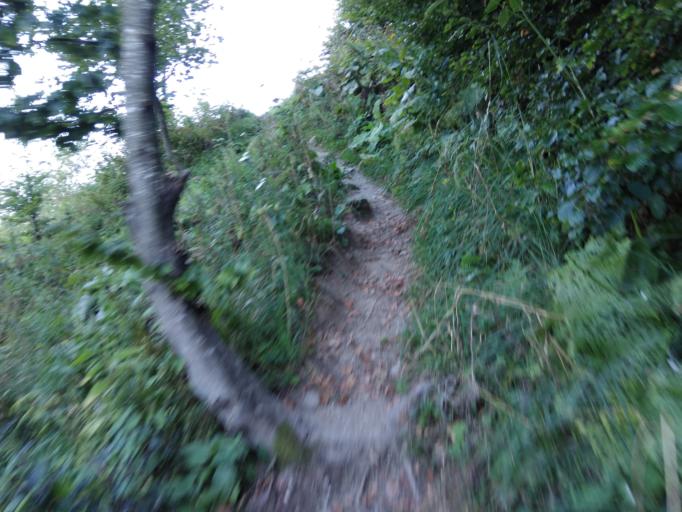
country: BG
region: Stara Zagora
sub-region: Obshtina Pavel Banya
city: Asen
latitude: 42.7596
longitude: 25.1134
